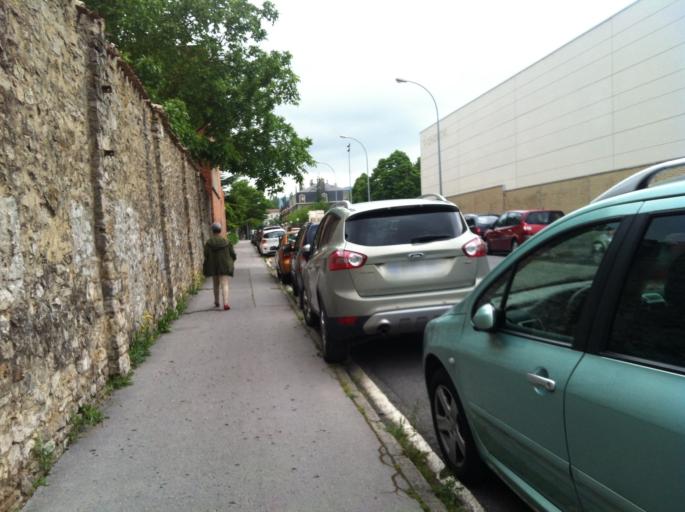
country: ES
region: Basque Country
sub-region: Provincia de Alava
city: Gasteiz / Vitoria
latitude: 42.8402
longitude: -2.6777
